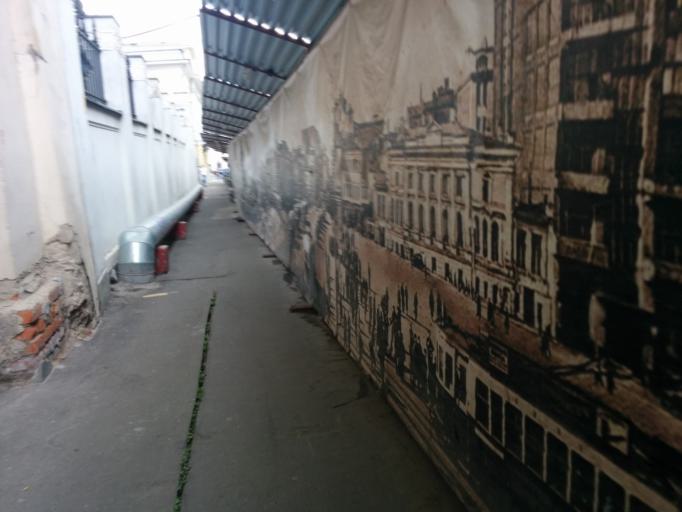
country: RU
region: Moscow
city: Moscow
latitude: 55.7477
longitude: 37.6054
